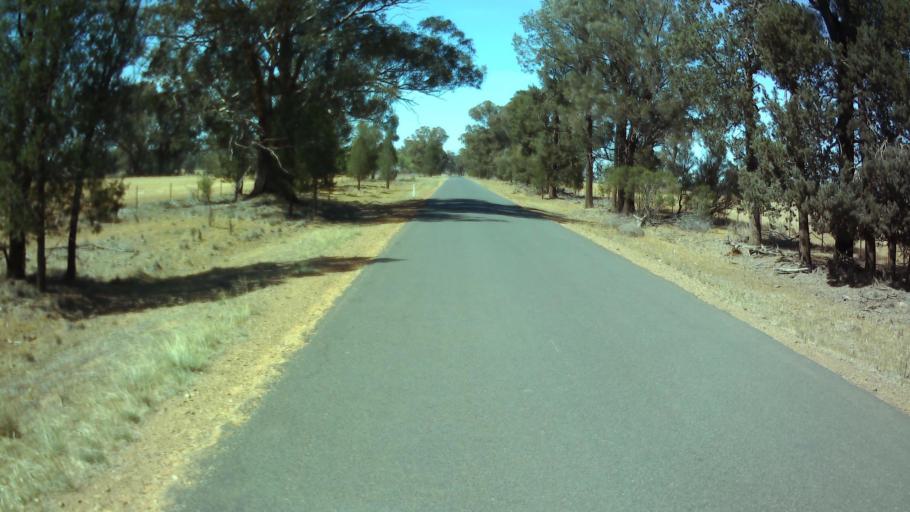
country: AU
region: New South Wales
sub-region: Weddin
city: Grenfell
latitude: -34.1122
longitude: 147.8854
